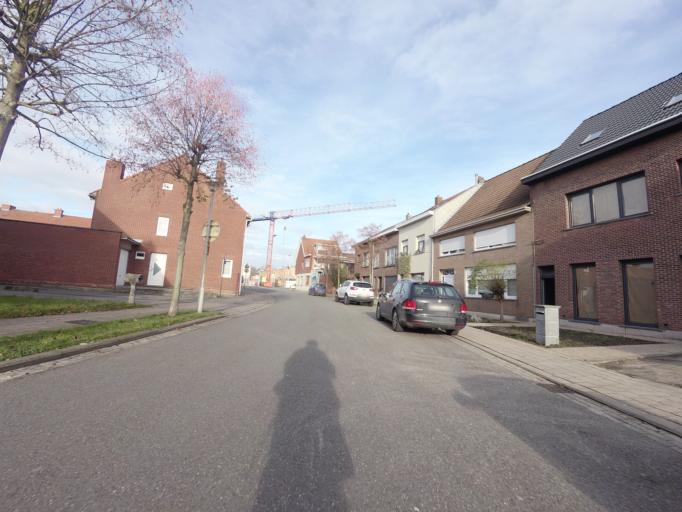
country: BE
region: Flanders
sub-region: Provincie Antwerpen
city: Schelle
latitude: 51.1259
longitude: 4.3327
